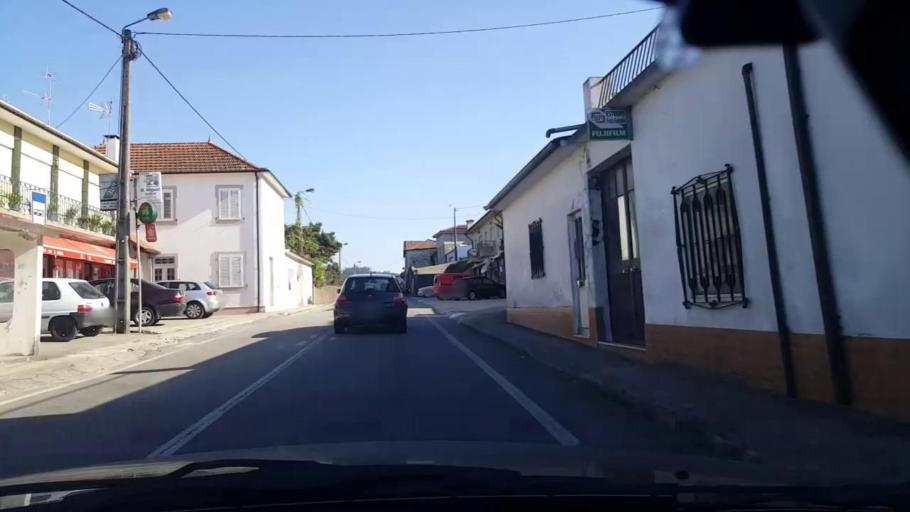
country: PT
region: Porto
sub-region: Vila do Conde
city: Arvore
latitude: 41.3320
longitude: -8.6634
